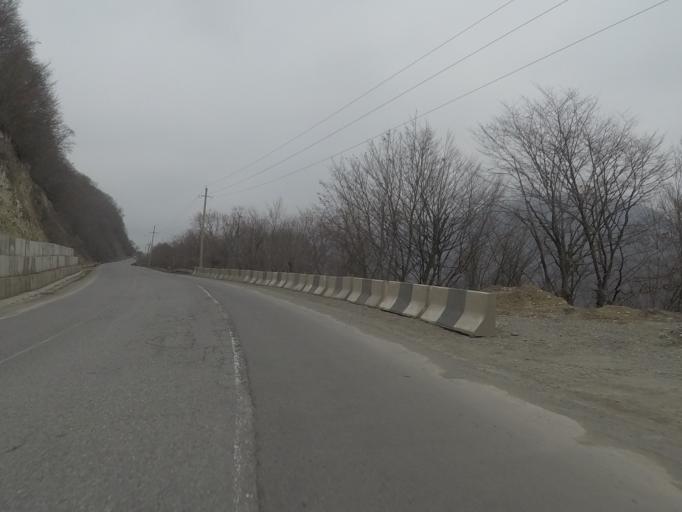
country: GE
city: Zhinvali
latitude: 42.1488
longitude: 44.7621
